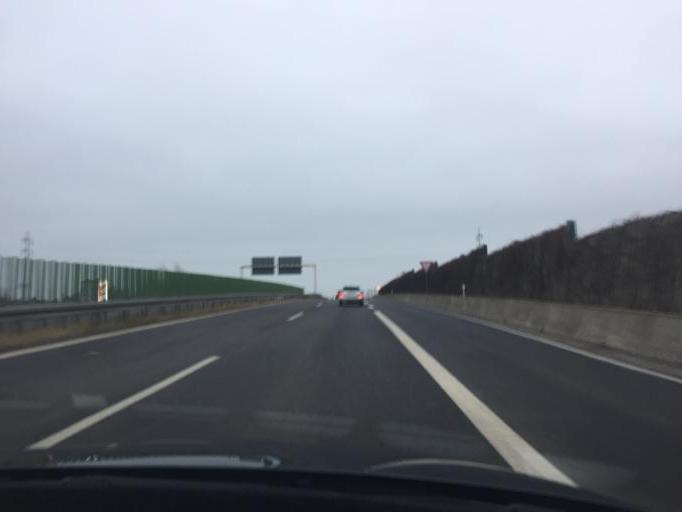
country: DE
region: Berlin
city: Lichtenrade
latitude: 52.3578
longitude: 13.4306
